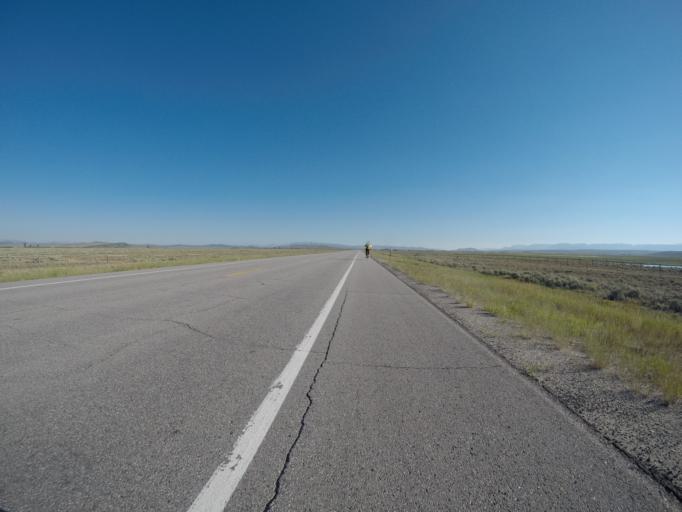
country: US
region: Wyoming
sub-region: Sublette County
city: Pinedale
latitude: 42.9584
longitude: -110.0875
